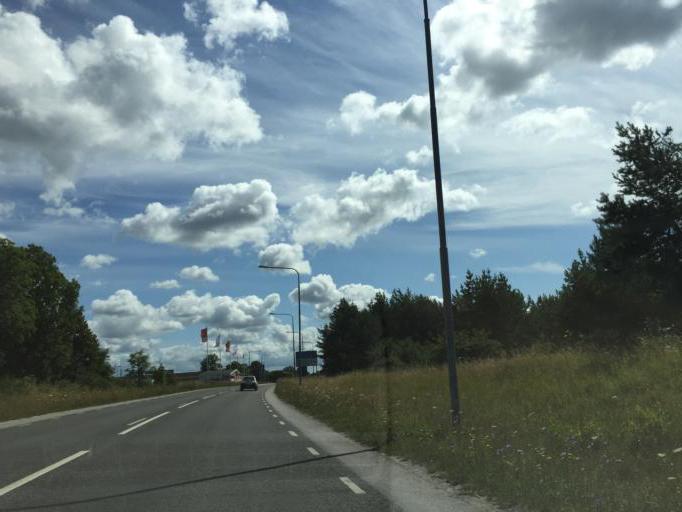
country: SE
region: Gotland
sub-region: Gotland
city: Visby
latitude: 57.6190
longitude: 18.2823
